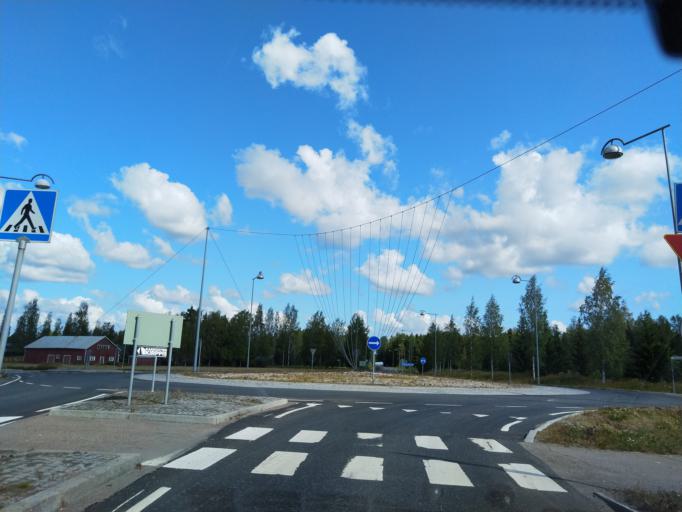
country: FI
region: Satakunta
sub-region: Pori
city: Huittinen
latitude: 61.1730
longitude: 22.7093
